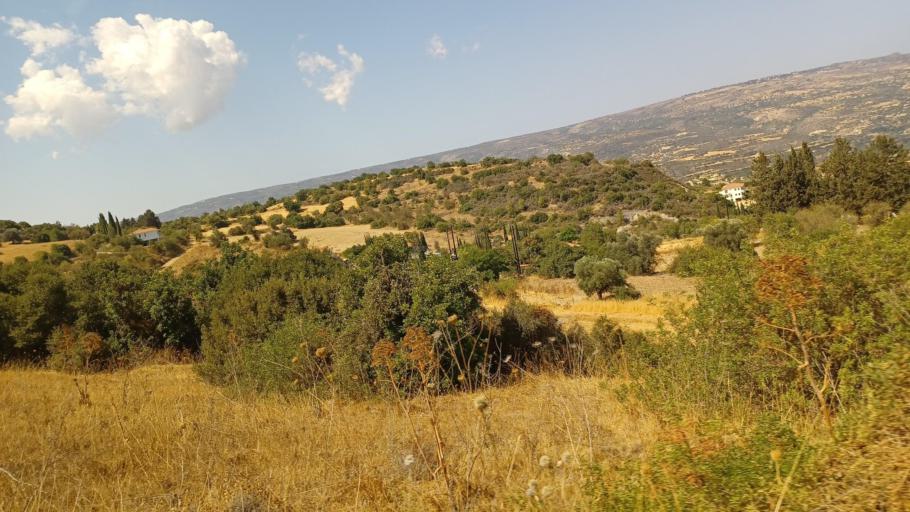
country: CY
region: Pafos
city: Polis
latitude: 34.9861
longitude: 32.4907
